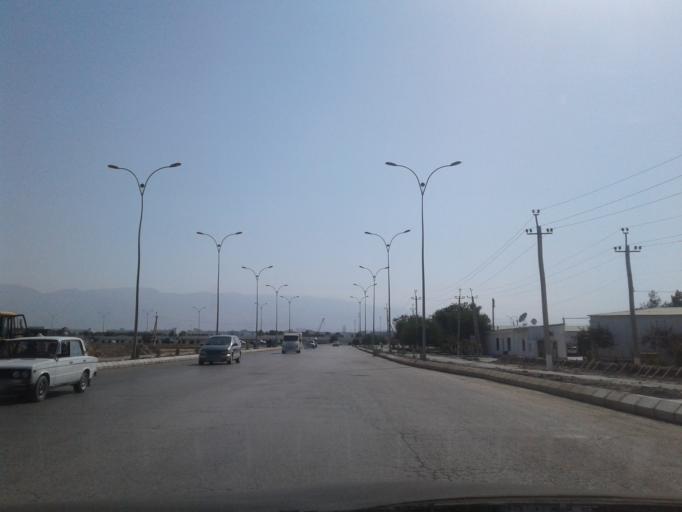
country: TM
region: Ahal
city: Ashgabat
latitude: 37.9710
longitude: 58.4249
